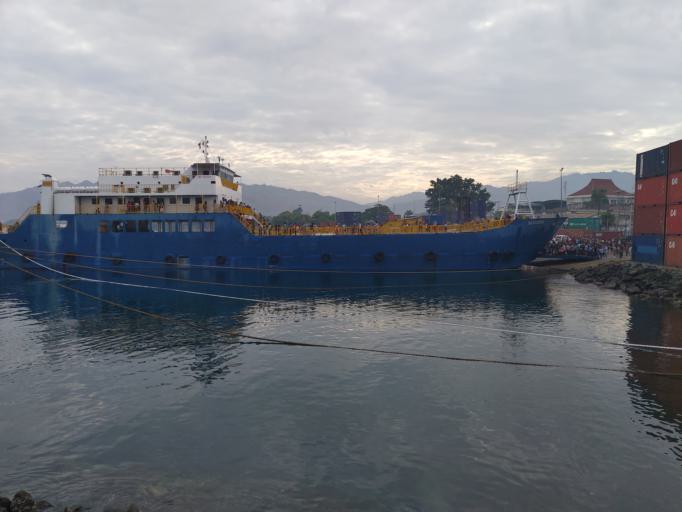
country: TL
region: Dili
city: Dili
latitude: -8.5534
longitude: 125.5746
